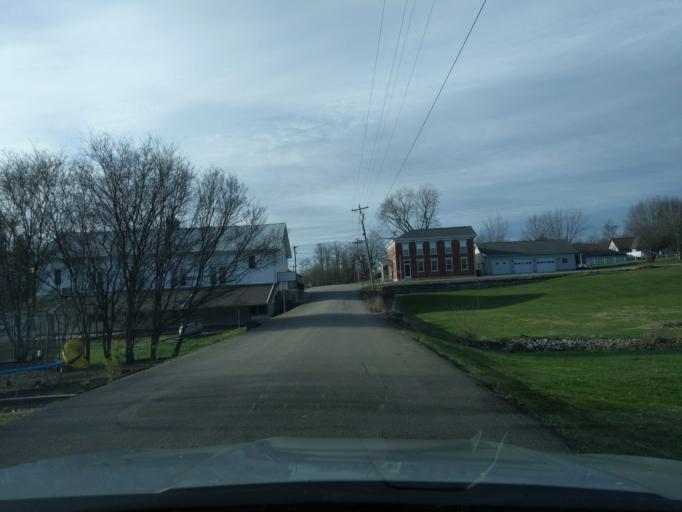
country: US
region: Indiana
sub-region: Decatur County
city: Greensburg
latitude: 39.2100
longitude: -85.4341
